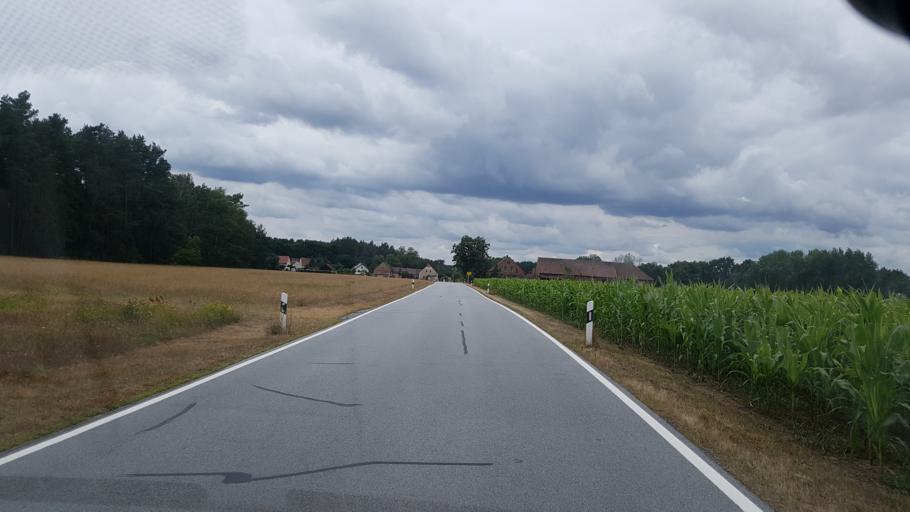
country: DE
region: Saxony
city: Mucka
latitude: 51.3774
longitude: 14.7210
